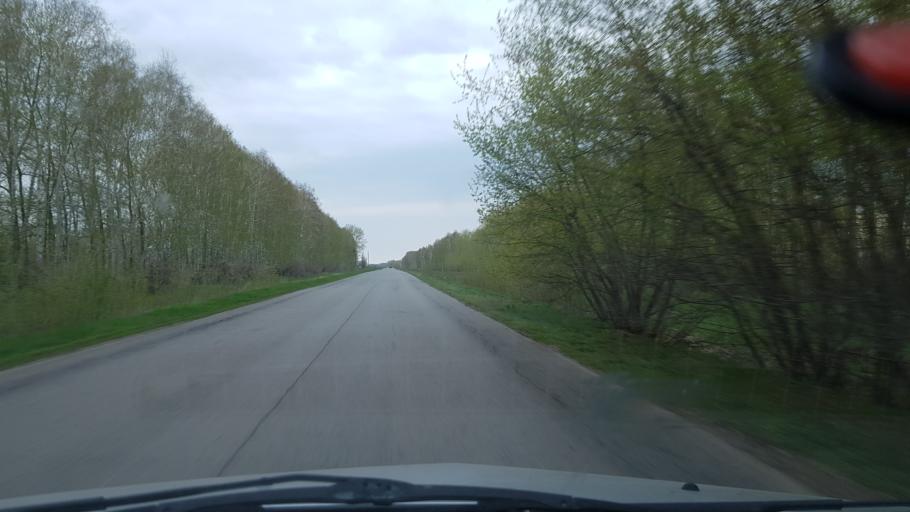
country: RU
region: Samara
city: Podstepki
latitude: 53.6652
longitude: 49.1724
